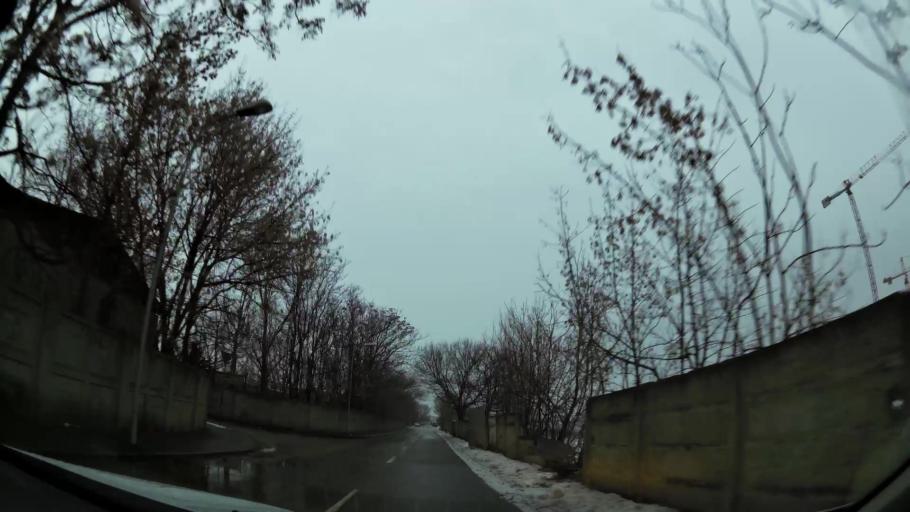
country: RO
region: Ilfov
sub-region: Comuna Chiajna
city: Rosu
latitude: 44.4754
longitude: 26.0538
